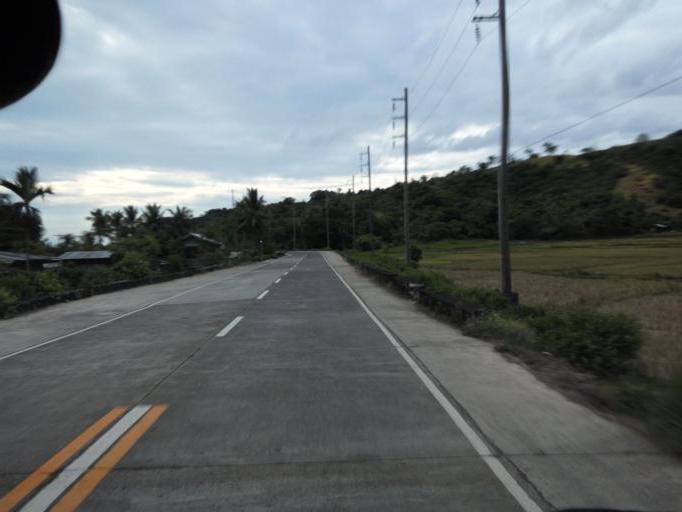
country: PH
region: Cagayan Valley
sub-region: Province of Cagayan
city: Casambalangan
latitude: 18.3929
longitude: 122.1382
